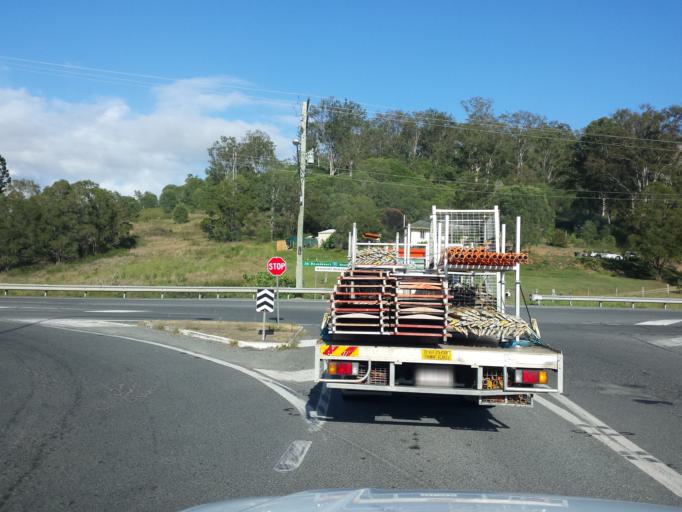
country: AU
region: Queensland
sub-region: Logan
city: Windaroo
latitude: -27.7744
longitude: 153.1861
